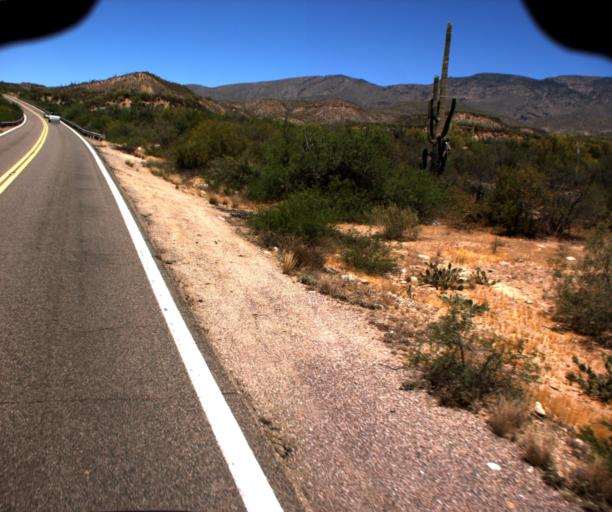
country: US
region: Arizona
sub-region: Pinal County
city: Kearny
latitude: 33.1257
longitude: -110.7754
